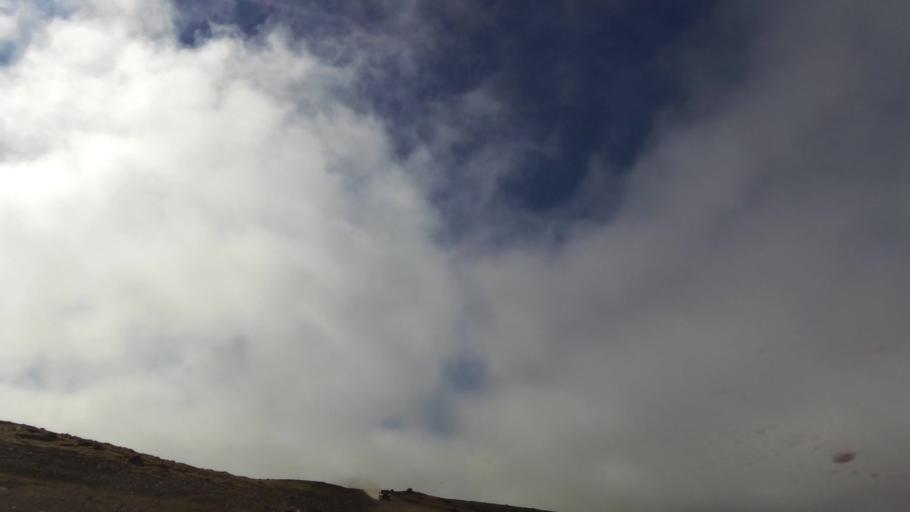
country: IS
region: West
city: Olafsvik
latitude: 65.5574
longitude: -24.2360
